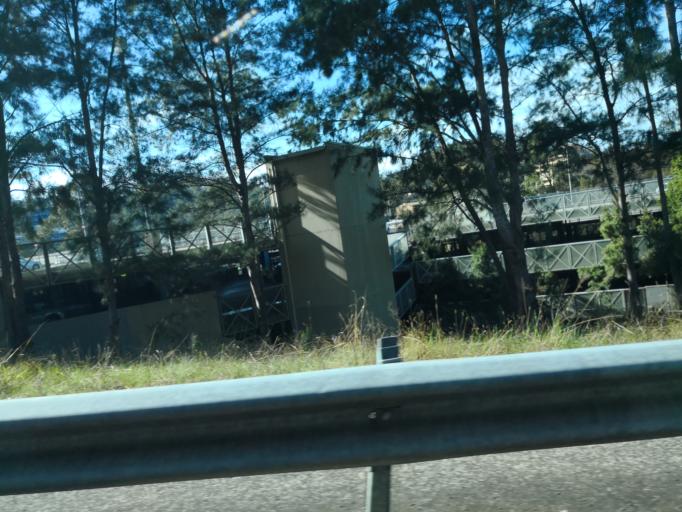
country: AU
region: New South Wales
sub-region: Gosford Shire
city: Gosford
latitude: -33.4252
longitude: 151.3397
